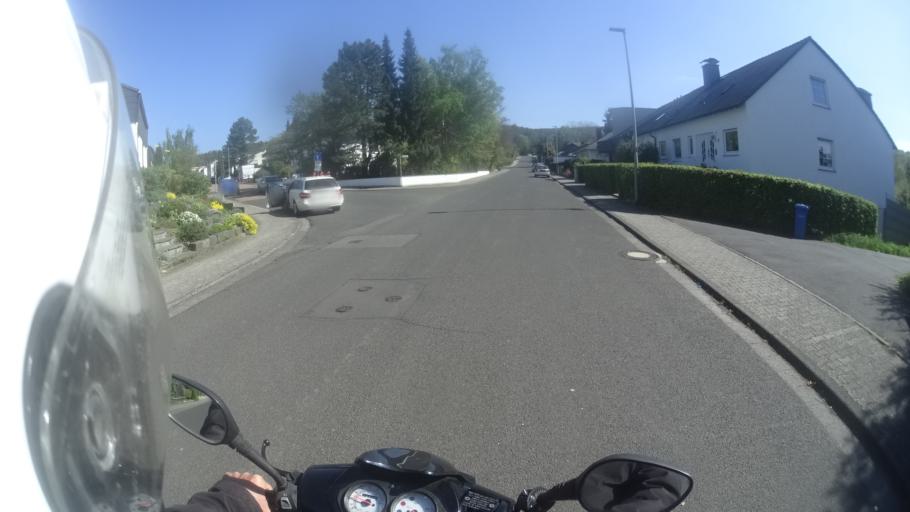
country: DE
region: Hesse
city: Taunusstein
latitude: 50.1312
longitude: 8.1383
